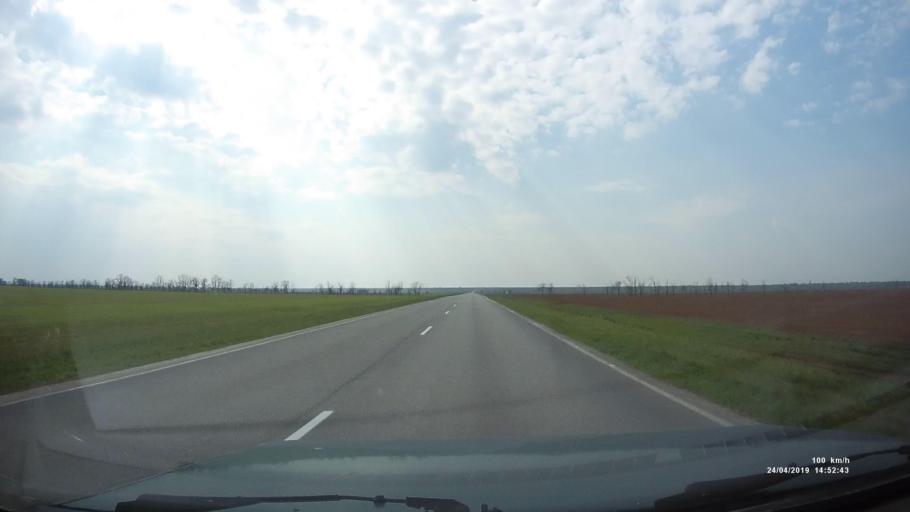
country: RU
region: Rostov
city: Remontnoye
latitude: 46.5306
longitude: 43.6749
